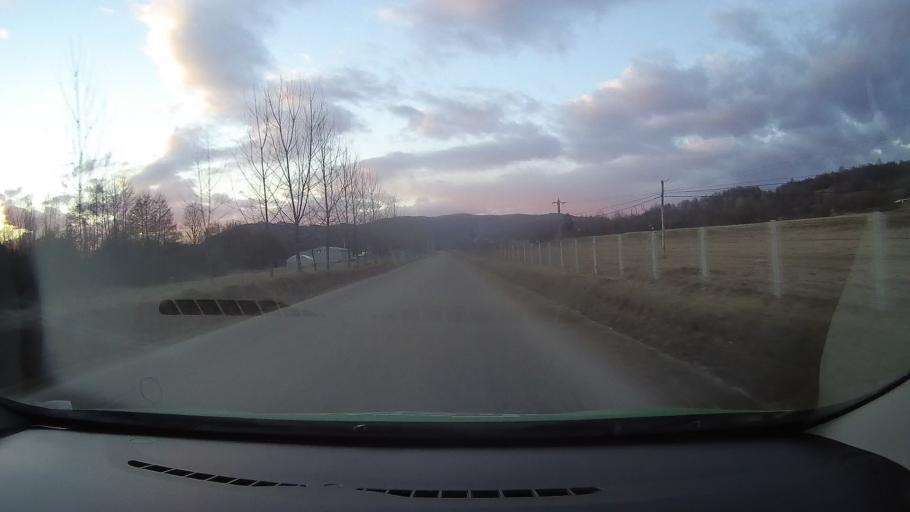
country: RO
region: Dambovita
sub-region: Comuna Valea Lunga
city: Valea Lunga Ogrea
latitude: 45.0622
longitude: 25.5896
